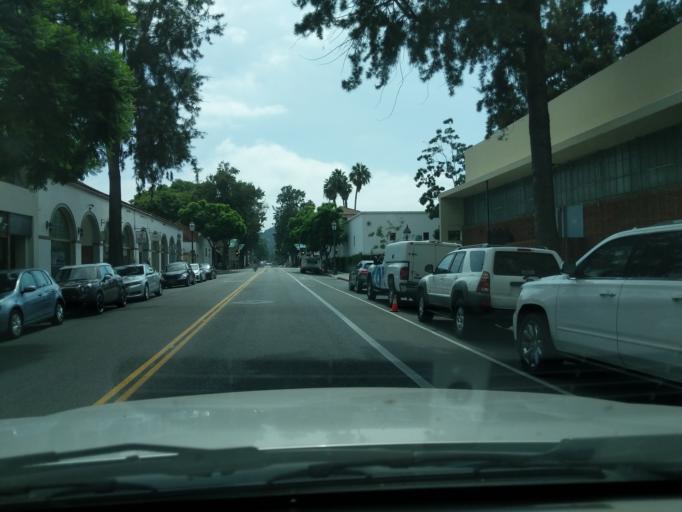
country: US
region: California
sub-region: Santa Barbara County
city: Santa Barbara
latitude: 34.4185
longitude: -119.6960
